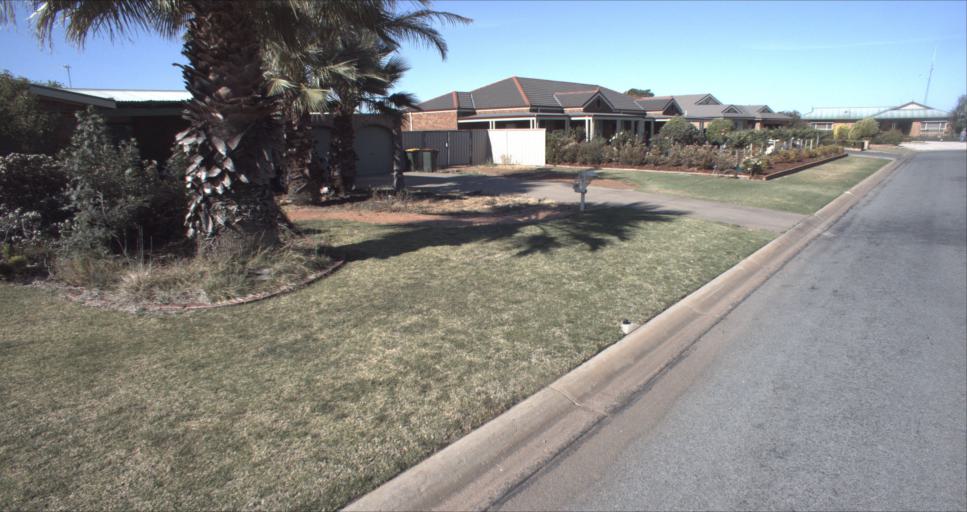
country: AU
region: New South Wales
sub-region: Leeton
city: Leeton
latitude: -34.5466
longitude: 146.4199
